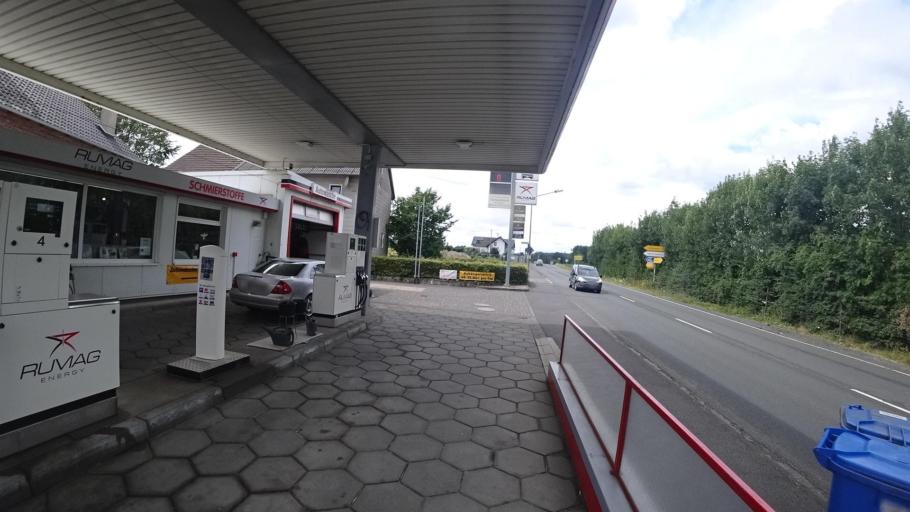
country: DE
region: Rheinland-Pfalz
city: Oberirsen
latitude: 50.7084
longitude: 7.5789
